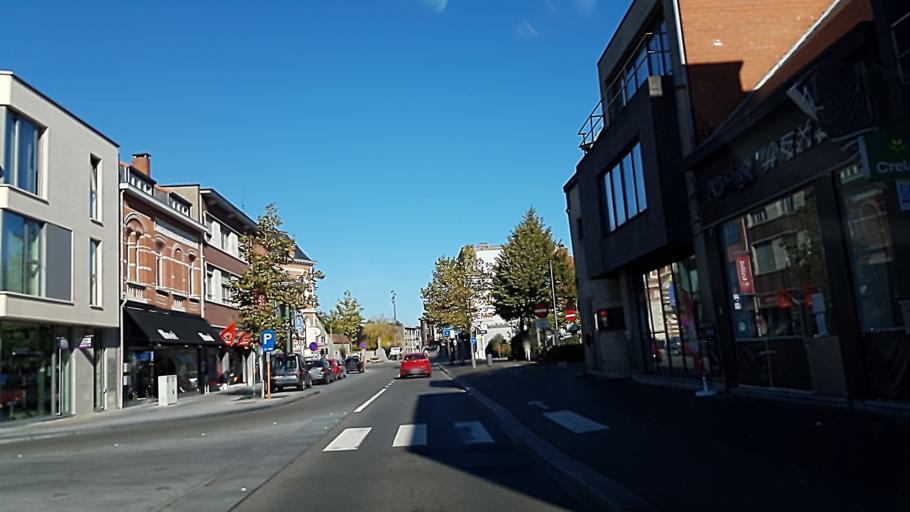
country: BE
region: Flanders
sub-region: Provincie Antwerpen
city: Kapellen
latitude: 51.3140
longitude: 4.4291
